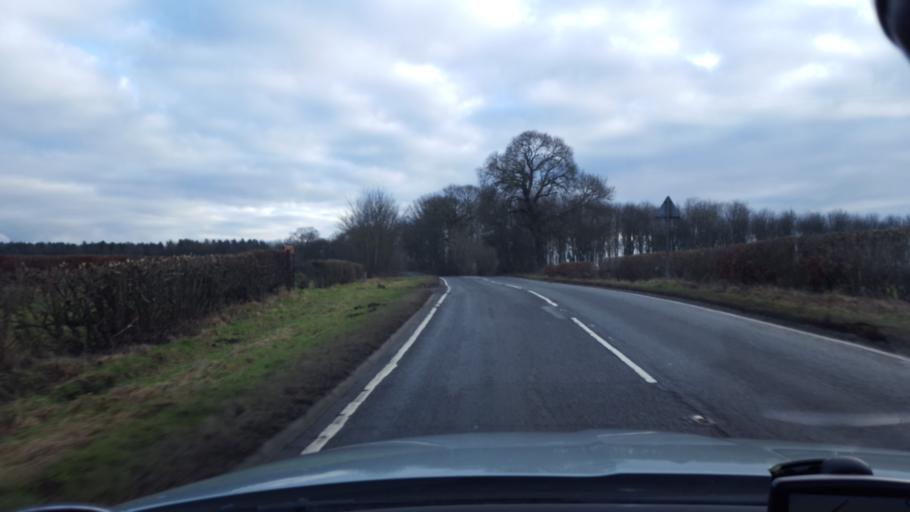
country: GB
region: Scotland
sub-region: West Lothian
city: Broxburn
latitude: 55.9733
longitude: -3.5086
